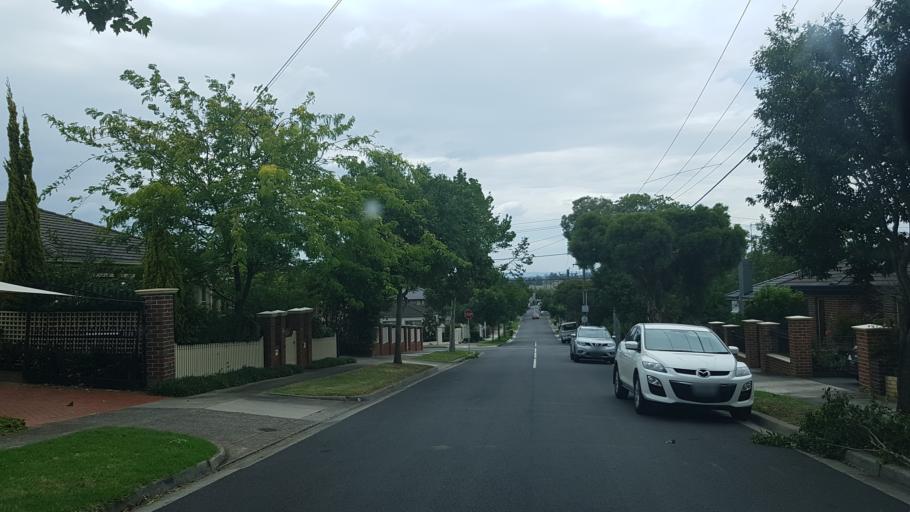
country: AU
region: Victoria
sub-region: Manningham
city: Bulleen
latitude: -37.7654
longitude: 145.0898
